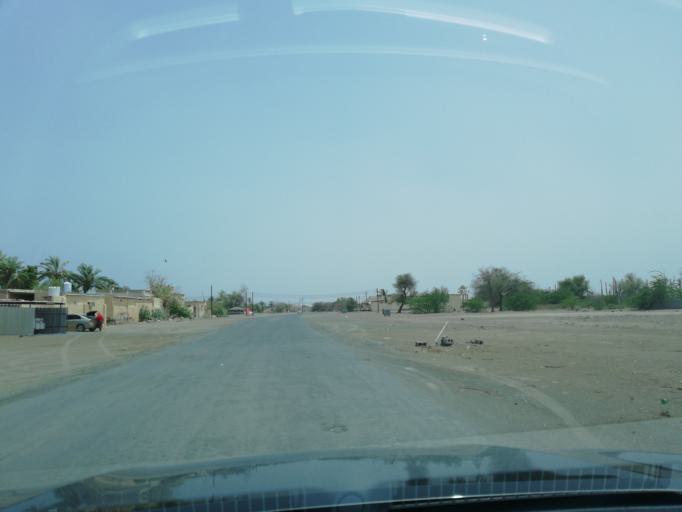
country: OM
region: Al Batinah
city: Al Liwa'
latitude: 24.6206
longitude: 56.5334
